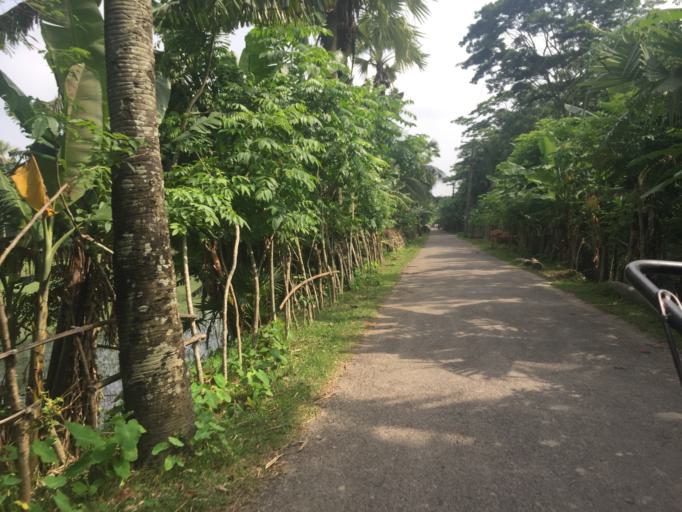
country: BD
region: Barisal
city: Mathba
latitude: 22.2368
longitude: 89.9152
